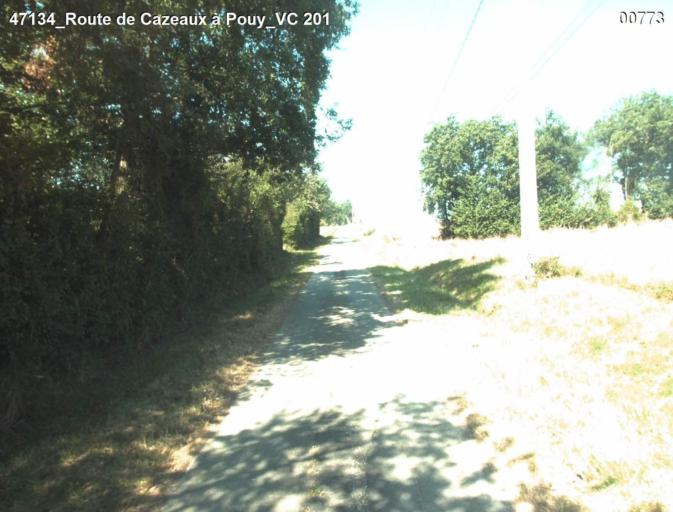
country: FR
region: Aquitaine
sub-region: Departement du Lot-et-Garonne
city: Mezin
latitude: 44.0150
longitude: 0.3000
